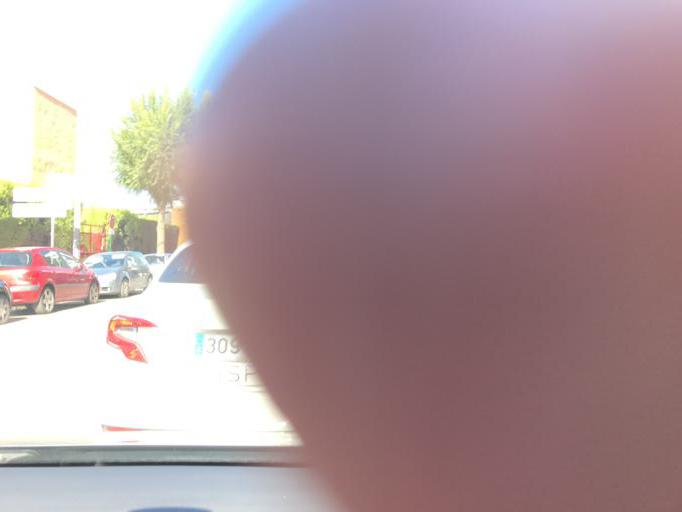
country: ES
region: Andalusia
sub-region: Provincia de Granada
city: Granada
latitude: 37.1727
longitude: -3.6090
